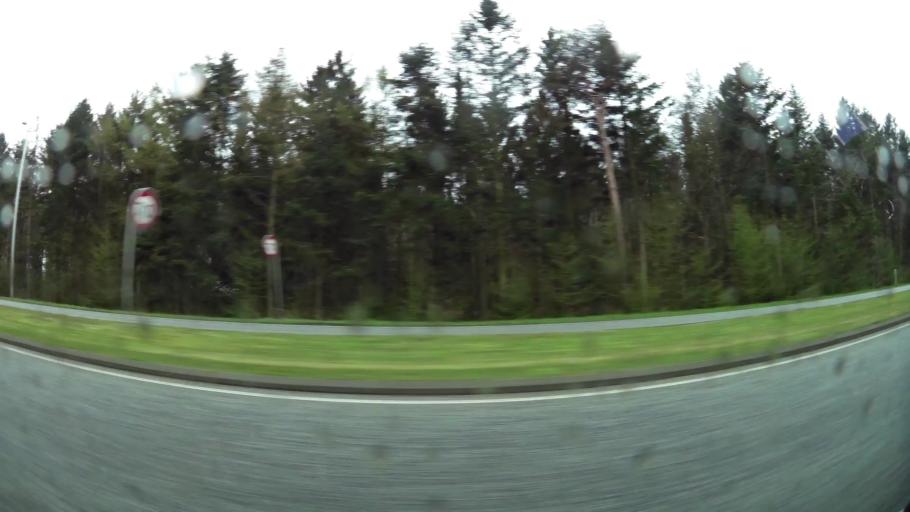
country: DK
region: Central Jutland
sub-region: Holstebro Kommune
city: Holstebro
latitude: 56.3609
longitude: 8.6490
